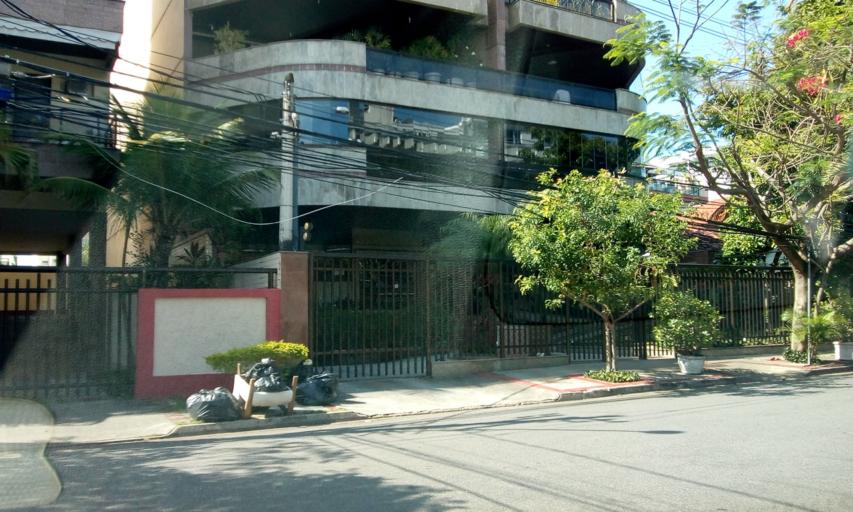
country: BR
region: Rio de Janeiro
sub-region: Nilopolis
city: Nilopolis
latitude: -23.0189
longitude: -43.4573
